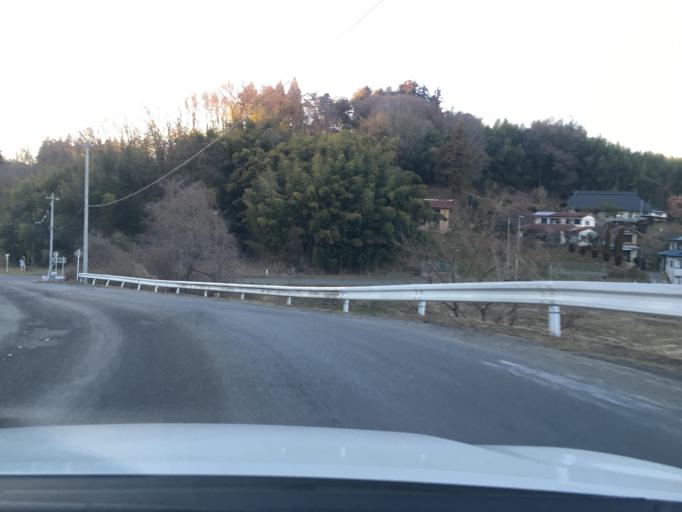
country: JP
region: Fukushima
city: Miharu
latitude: 37.4601
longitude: 140.4992
